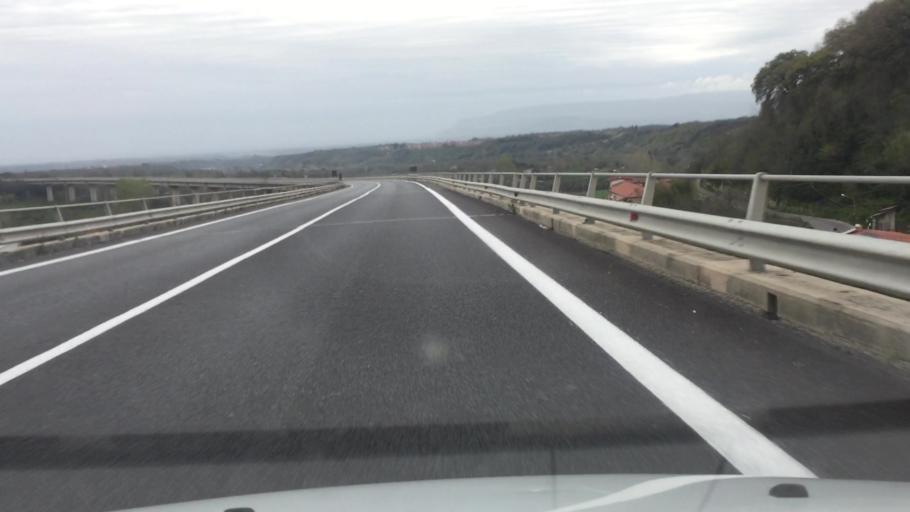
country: IT
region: Calabria
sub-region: Provincia di Reggio Calabria
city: Anoia Superiore
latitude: 38.4192
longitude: 16.1018
